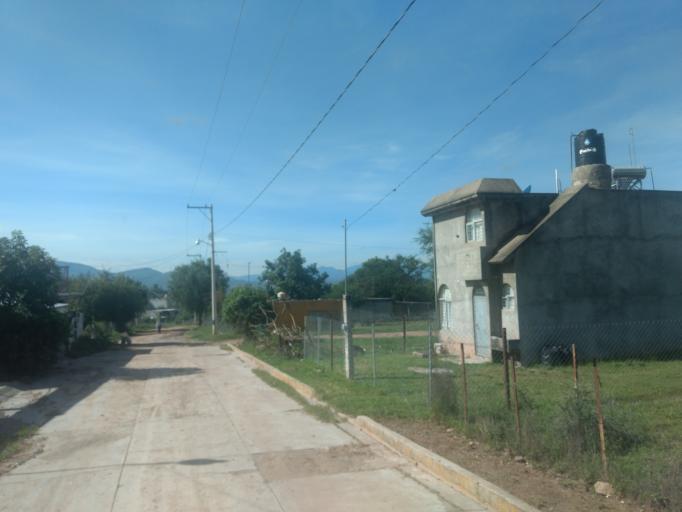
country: MX
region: Oaxaca
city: Ciudad de Huajuapam de Leon
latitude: 17.8236
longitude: -97.7864
